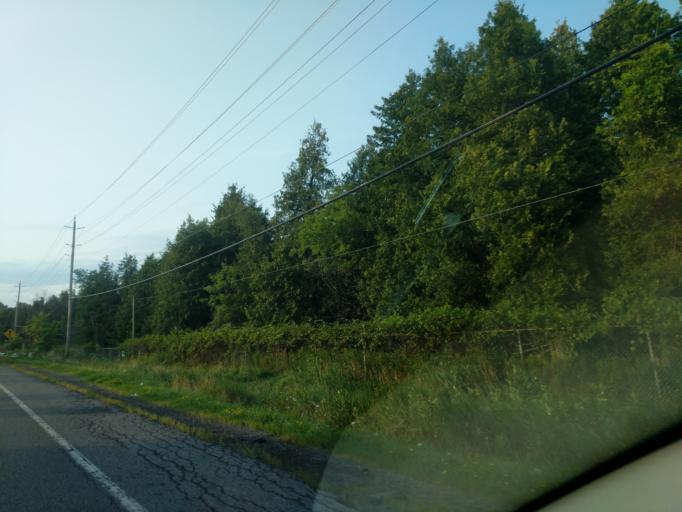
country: CA
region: Ontario
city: Bells Corners
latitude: 45.2848
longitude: -75.7835
